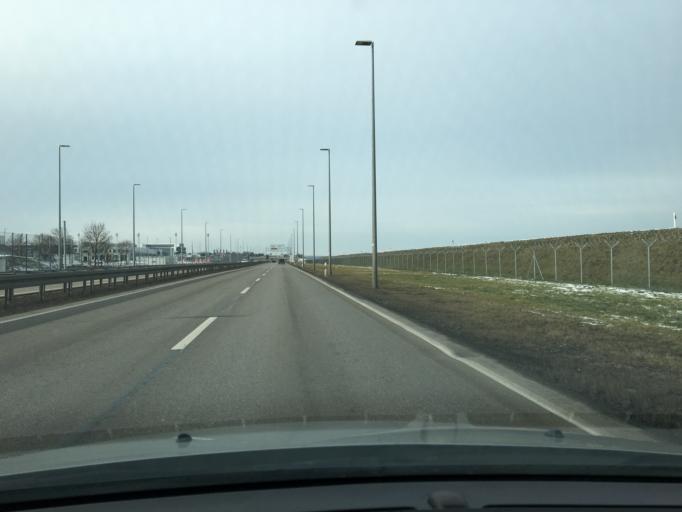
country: DE
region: Bavaria
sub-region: Upper Bavaria
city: Marzling
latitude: 48.3607
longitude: 11.8020
